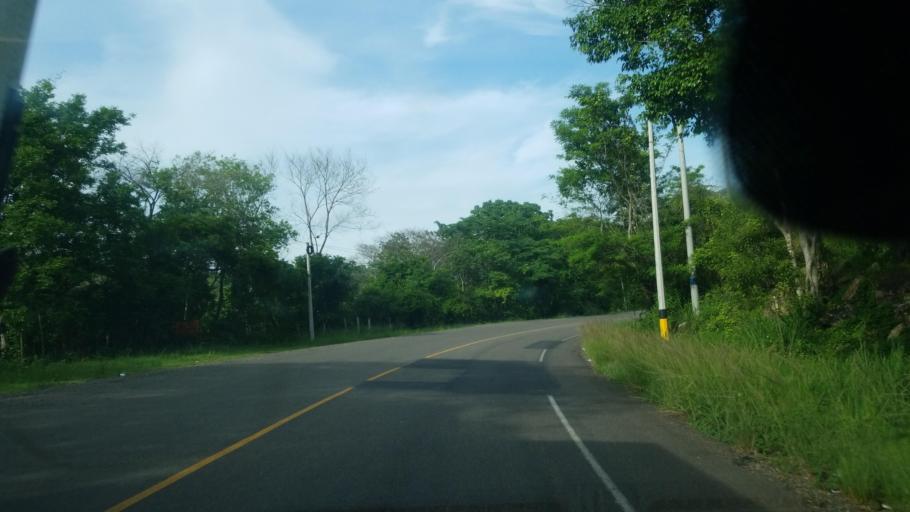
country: HN
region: Santa Barbara
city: Trinidad
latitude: 15.1405
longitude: -88.2403
